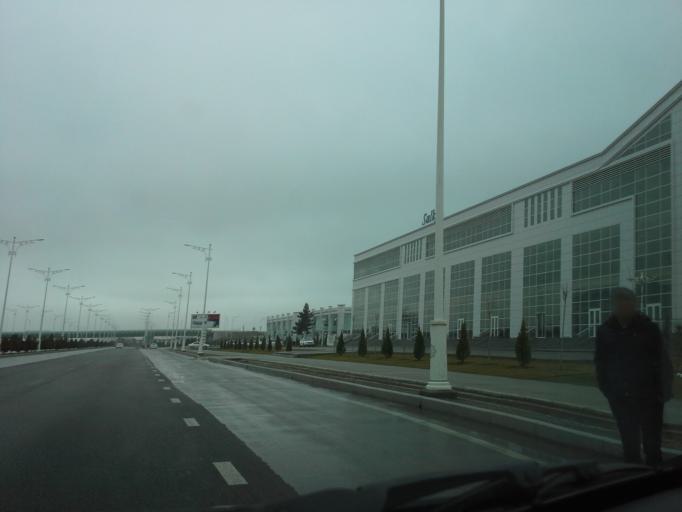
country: TM
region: Ahal
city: Ashgabat
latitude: 37.9631
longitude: 58.4143
